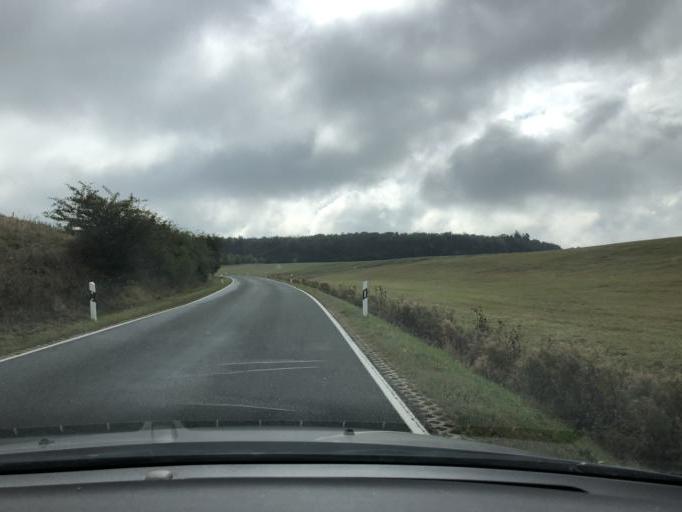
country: DE
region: Thuringia
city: Heuthen
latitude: 51.3216
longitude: 10.2194
